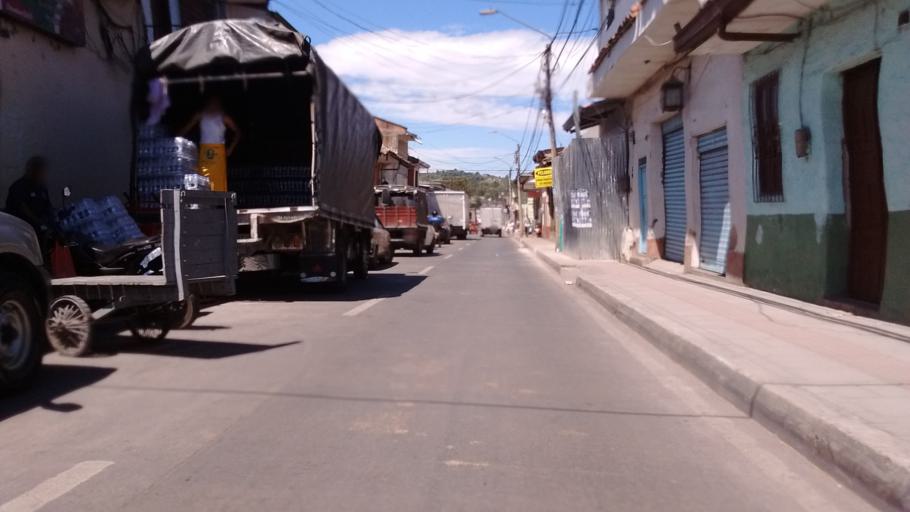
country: CO
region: Cauca
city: Popayan
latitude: 2.4379
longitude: -76.6053
